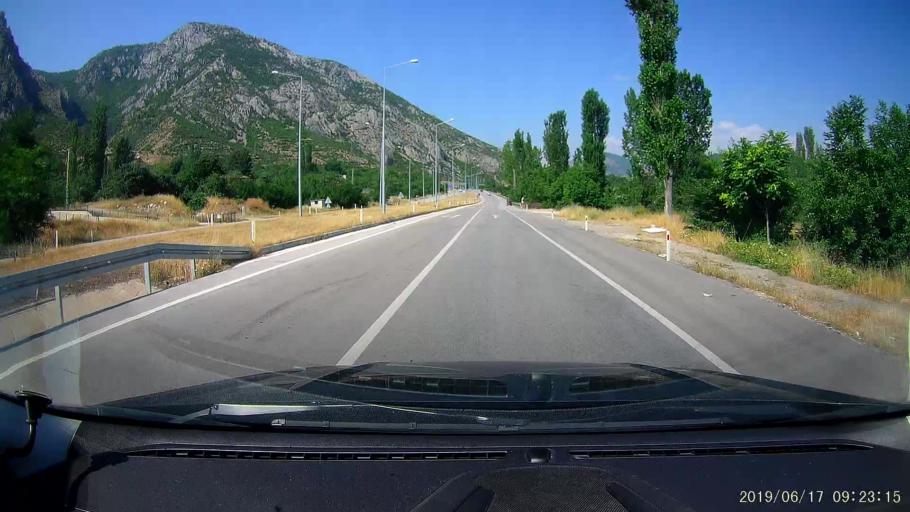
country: TR
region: Amasya
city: Amasya
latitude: 40.6778
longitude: 35.8777
